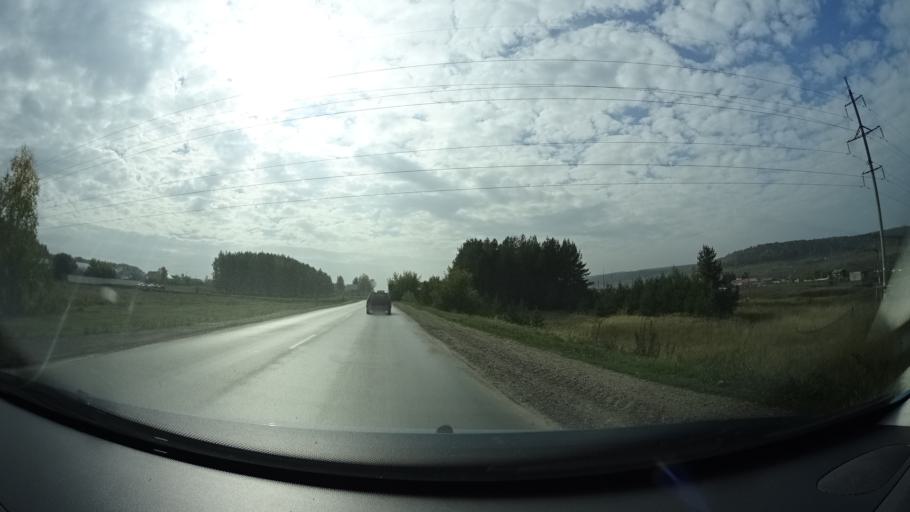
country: RU
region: Bashkortostan
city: Oktyabr'skiy
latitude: 54.5225
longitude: 53.5427
